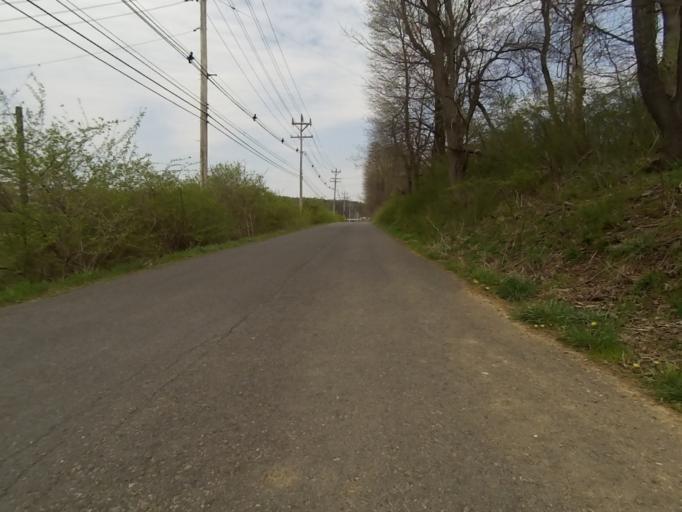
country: US
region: Pennsylvania
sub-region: Centre County
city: State College
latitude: 40.8187
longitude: -77.8722
